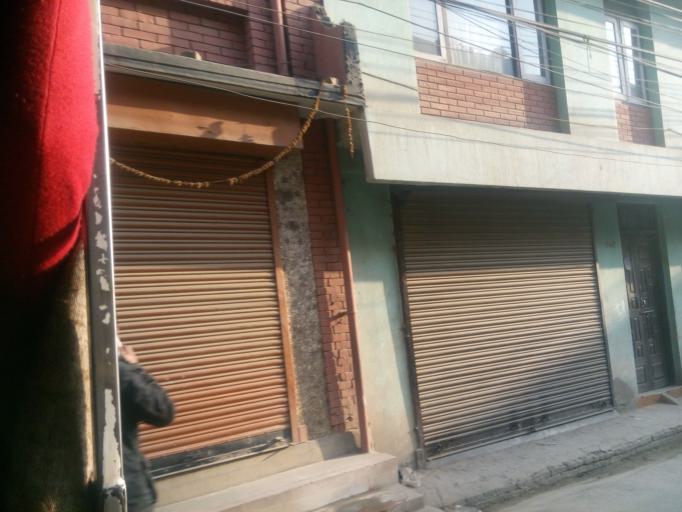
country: NP
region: Central Region
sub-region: Bagmati Zone
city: Patan
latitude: 27.6671
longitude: 85.3288
